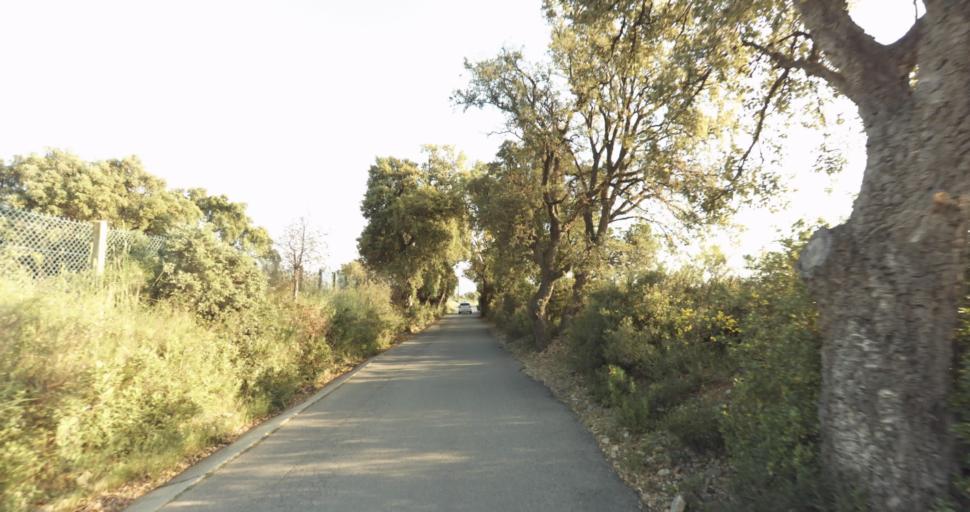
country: FR
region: Corsica
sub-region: Departement de la Haute-Corse
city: Biguglia
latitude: 42.6051
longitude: 9.4443
